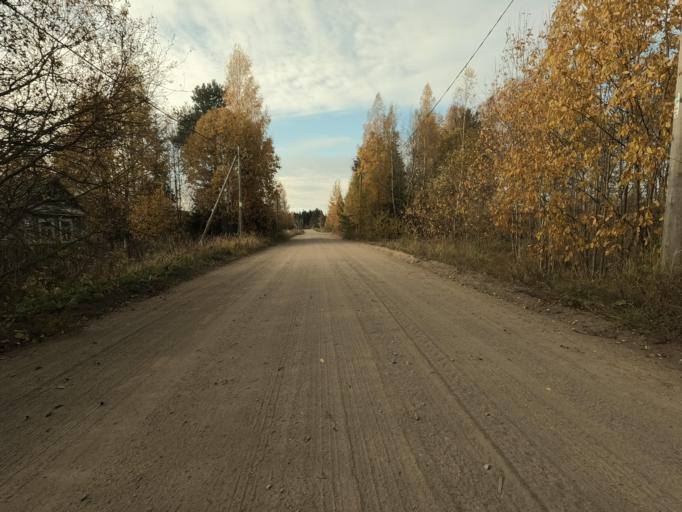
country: RU
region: Leningrad
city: Priladozhskiy
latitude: 59.6296
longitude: 31.4035
